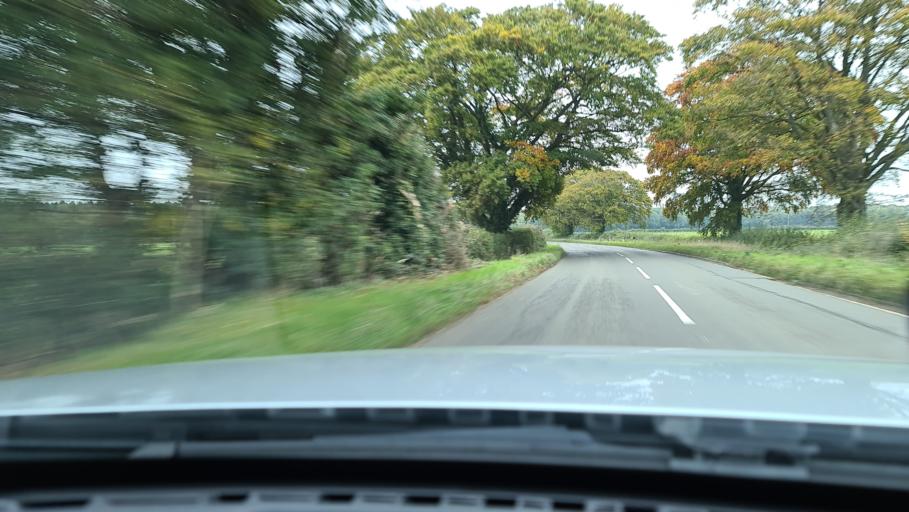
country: GB
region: England
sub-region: Oxfordshire
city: Somerton
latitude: 51.9203
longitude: -1.2402
